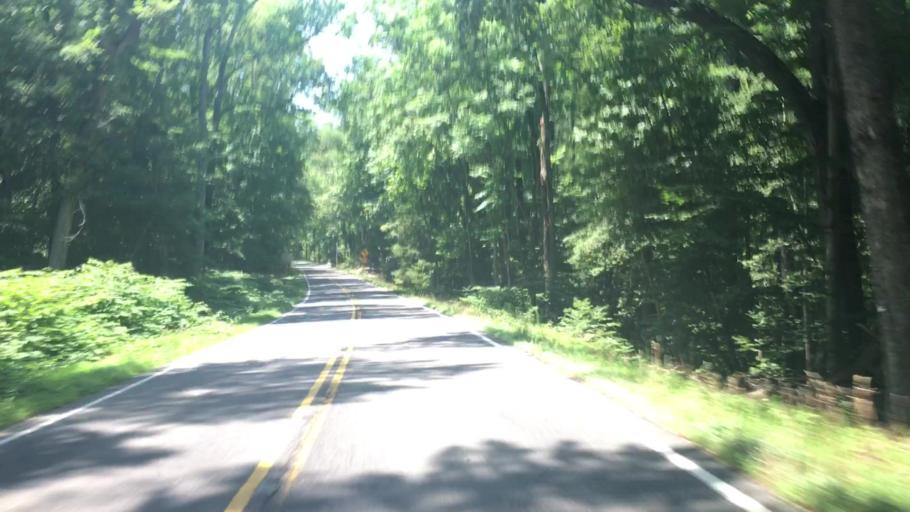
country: US
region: Virginia
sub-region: King George County
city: Dahlgren
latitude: 38.3353
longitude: -77.1317
